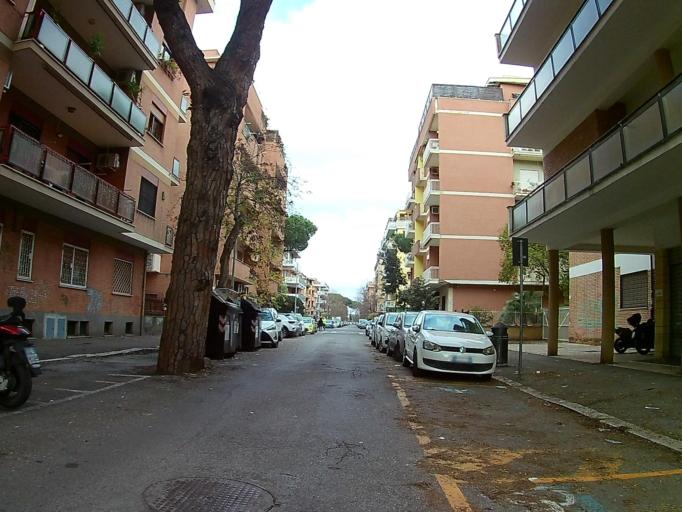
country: IT
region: Latium
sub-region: Citta metropolitana di Roma Capitale
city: Lido di Ostia
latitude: 41.7322
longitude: 12.2878
